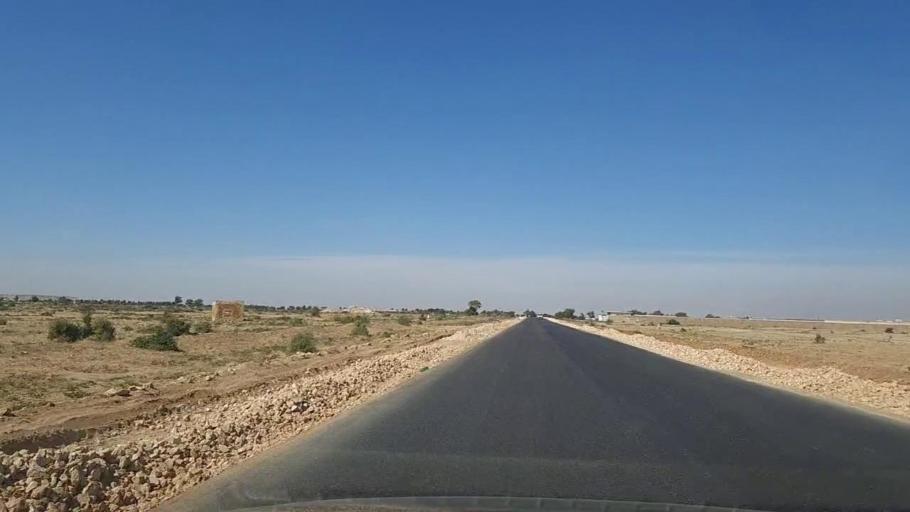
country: PK
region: Sindh
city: Kotri
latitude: 25.2772
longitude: 68.2139
